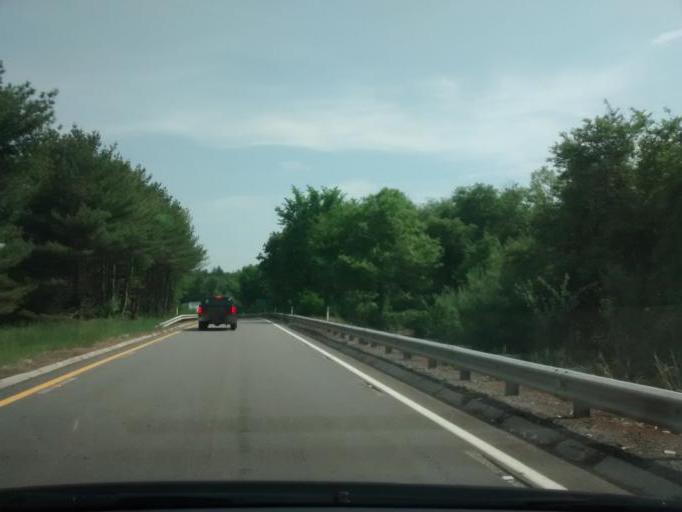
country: US
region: Massachusetts
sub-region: Bristol County
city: Norton Center
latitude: 41.9828
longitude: -71.1618
